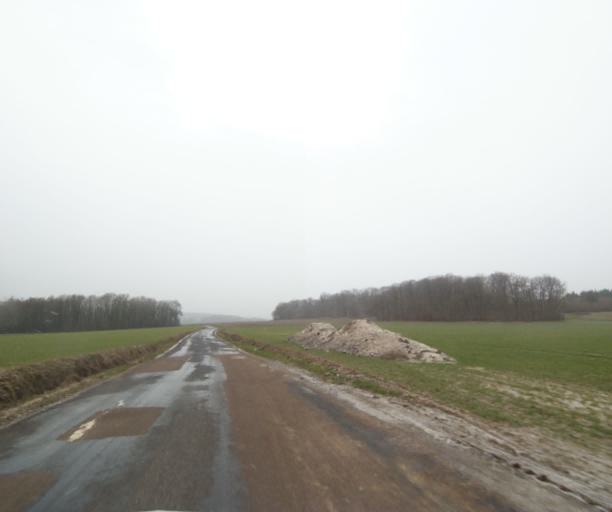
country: FR
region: Champagne-Ardenne
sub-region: Departement de la Haute-Marne
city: Bienville
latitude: 48.5262
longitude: 5.0425
